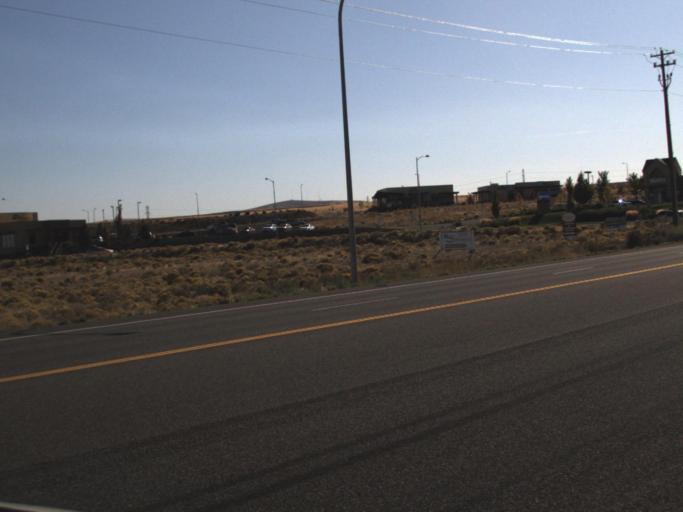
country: US
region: Washington
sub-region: Benton County
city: Kennewick
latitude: 46.1787
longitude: -119.1850
